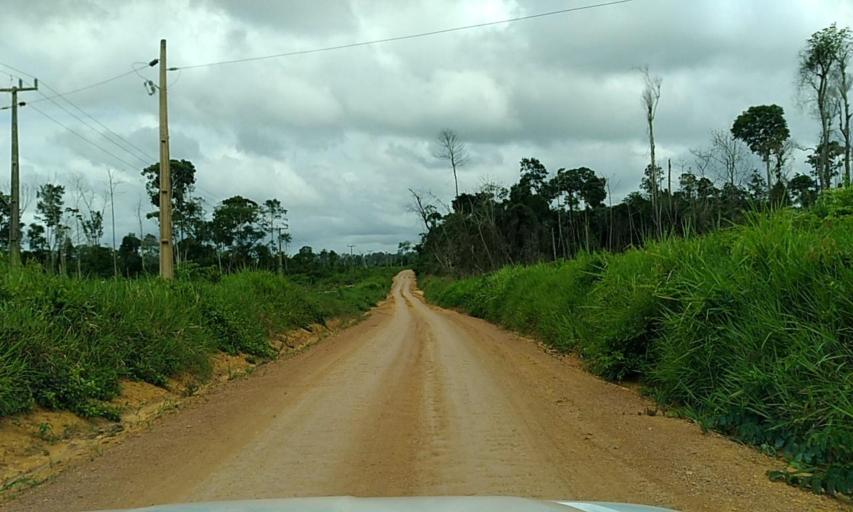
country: BR
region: Para
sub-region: Senador Jose Porfirio
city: Senador Jose Porfirio
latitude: -2.7677
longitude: -51.7833
